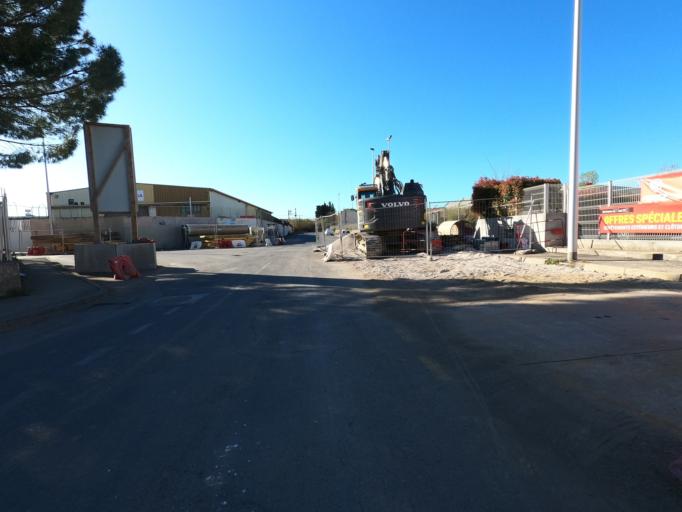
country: FR
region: Languedoc-Roussillon
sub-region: Departement de l'Herault
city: Montpellier
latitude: 43.5835
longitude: 3.8775
